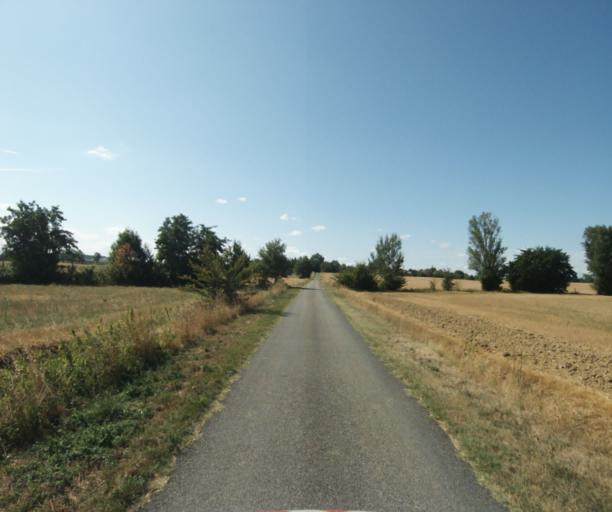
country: FR
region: Midi-Pyrenees
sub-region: Departement de la Haute-Garonne
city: Revel
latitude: 43.4969
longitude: 1.9840
